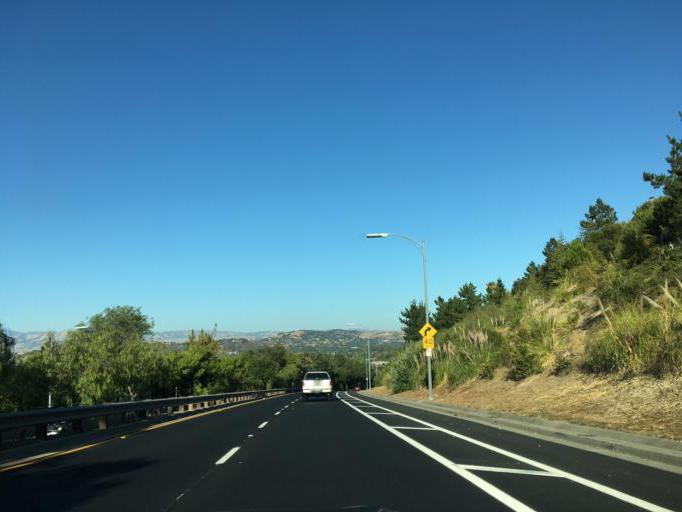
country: US
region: California
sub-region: Santa Clara County
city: Cambrian Park
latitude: 37.2213
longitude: -121.8922
